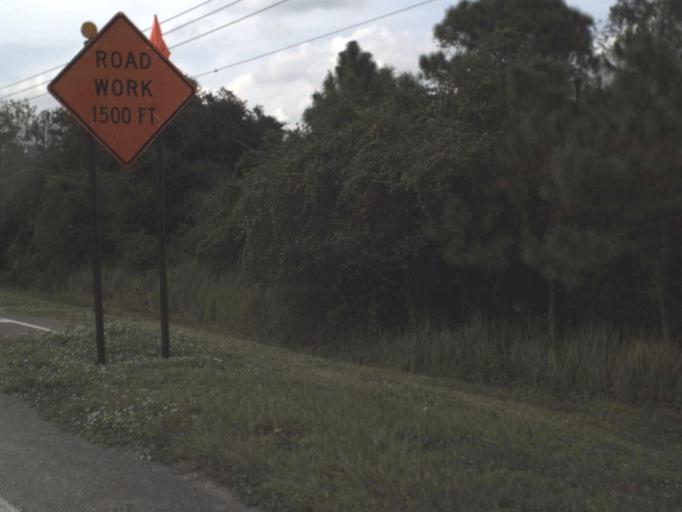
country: US
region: Florida
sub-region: Okeechobee County
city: Taylor Creek
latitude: 27.2378
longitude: -80.7824
